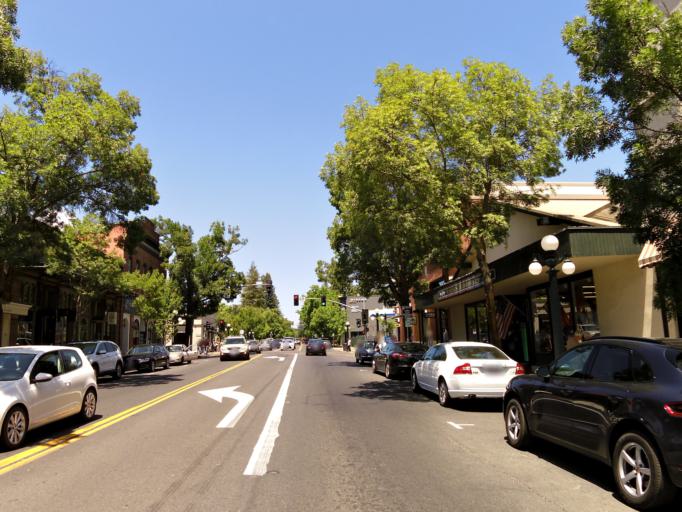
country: US
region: California
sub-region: Napa County
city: Saint Helena
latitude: 38.5050
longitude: -122.4698
